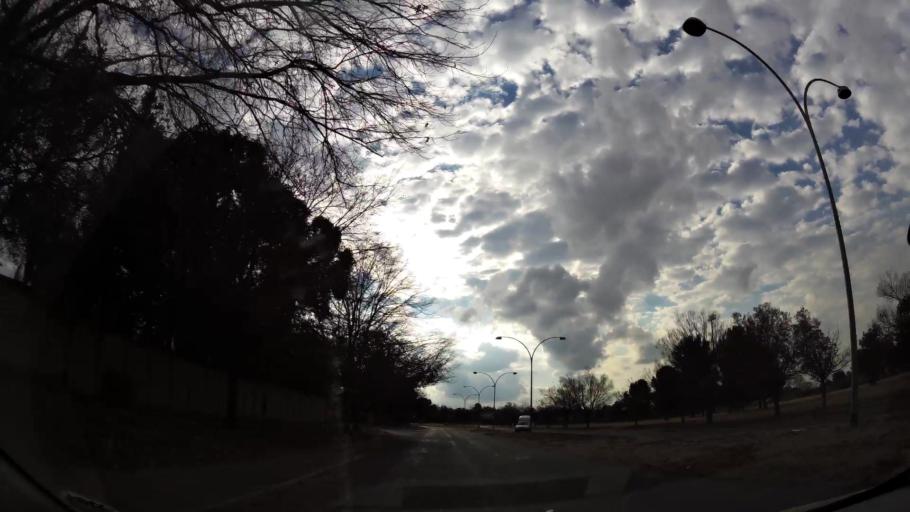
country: ZA
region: Orange Free State
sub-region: Fezile Dabi District Municipality
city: Sasolburg
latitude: -26.7974
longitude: 27.8263
